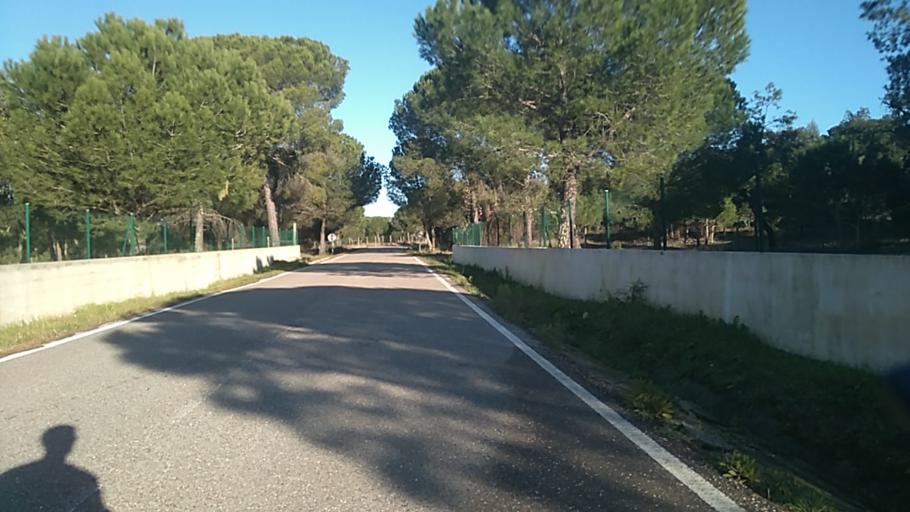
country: PT
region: Santarem
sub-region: Coruche
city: Coruche
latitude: 38.8311
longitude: -8.4612
